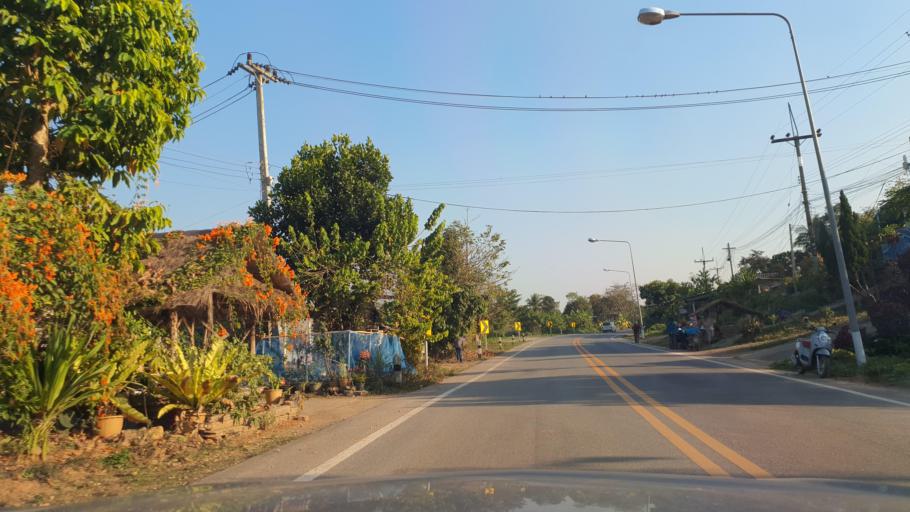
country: TH
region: Chiang Rai
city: Mae Lao
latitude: 19.8381
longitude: 99.6807
